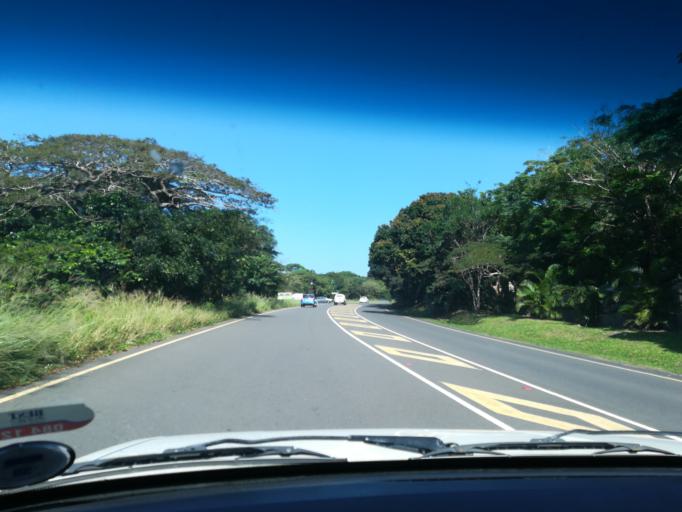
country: ZA
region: KwaZulu-Natal
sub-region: Ugu District Municipality
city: Scottburgh
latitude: -30.3792
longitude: 30.6906
